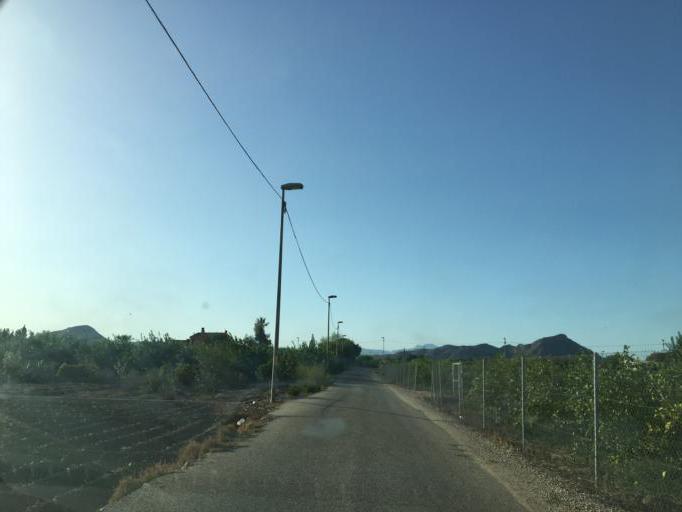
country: ES
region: Murcia
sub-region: Murcia
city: Santomera
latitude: 38.0232
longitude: -1.0573
